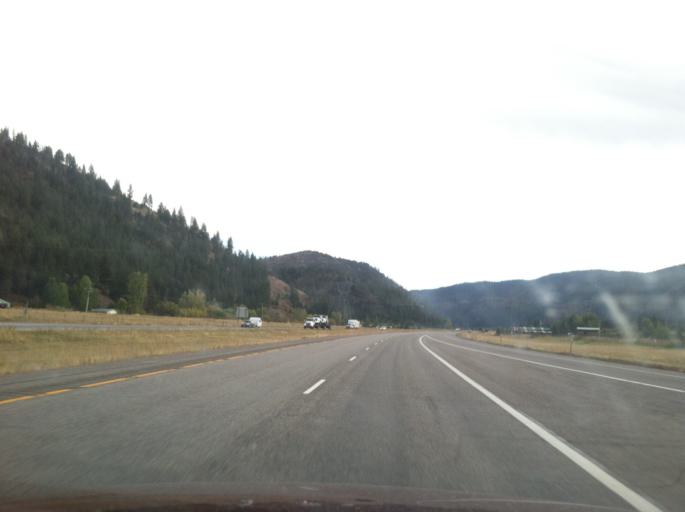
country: US
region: Montana
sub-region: Missoula County
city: Clinton
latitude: 46.7785
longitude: -113.7124
